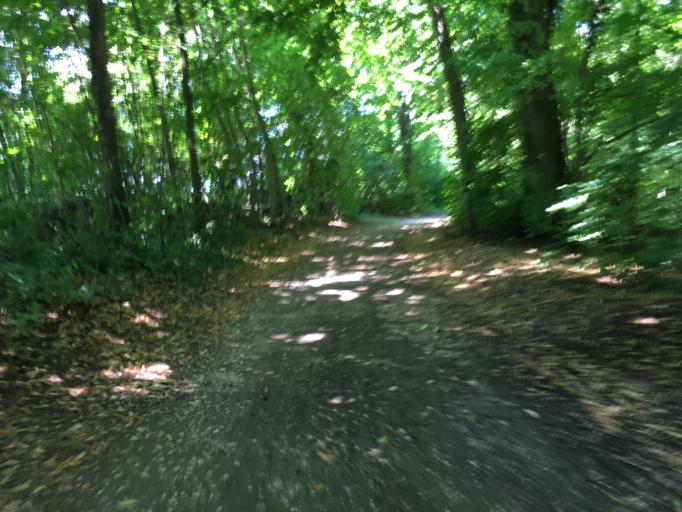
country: CH
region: Fribourg
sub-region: See District
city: Gurwolf
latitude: 46.9198
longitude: 7.0975
